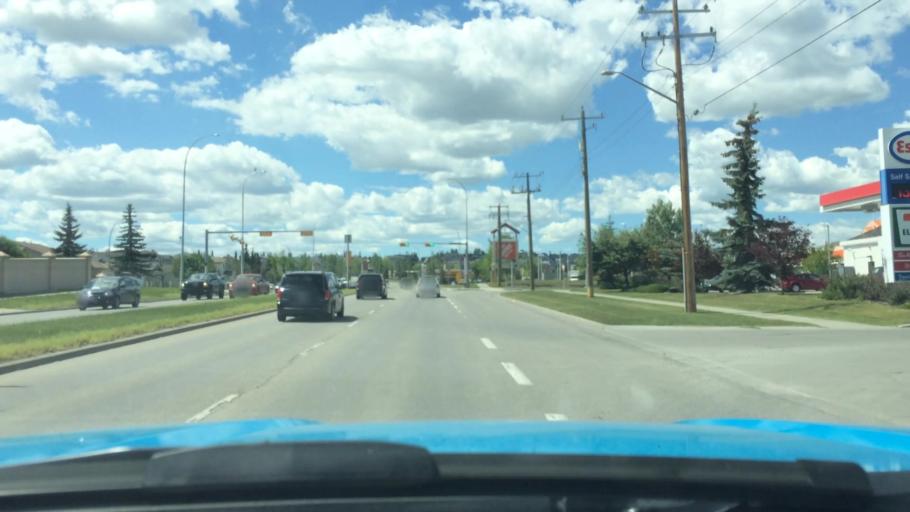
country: CA
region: Alberta
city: Calgary
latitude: 51.1543
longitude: -114.0595
